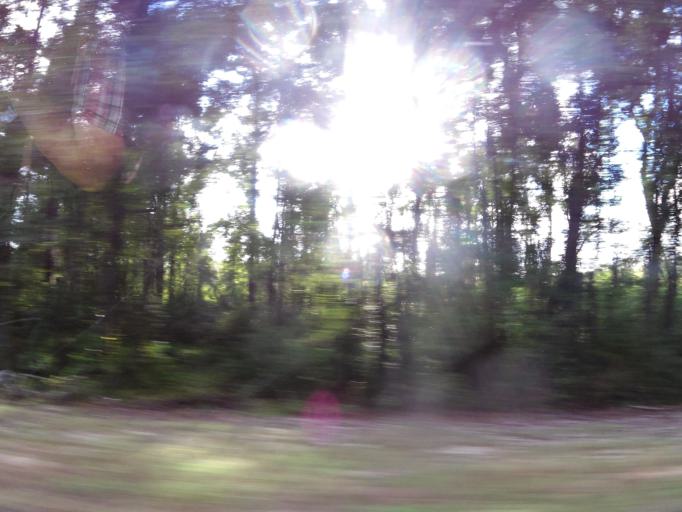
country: US
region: Georgia
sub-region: Liberty County
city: Midway
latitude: 31.6695
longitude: -81.4010
